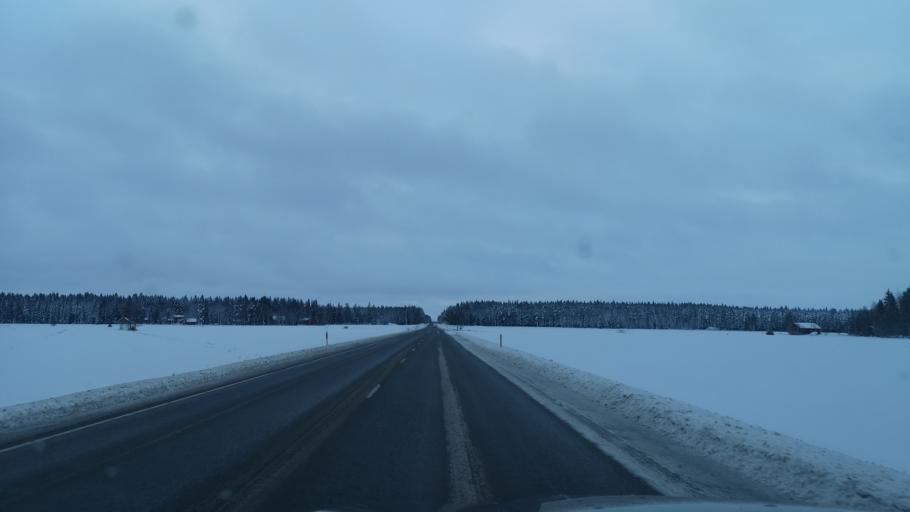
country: FI
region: Varsinais-Suomi
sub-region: Loimaa
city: Loimaa
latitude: 60.9083
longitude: 23.1616
